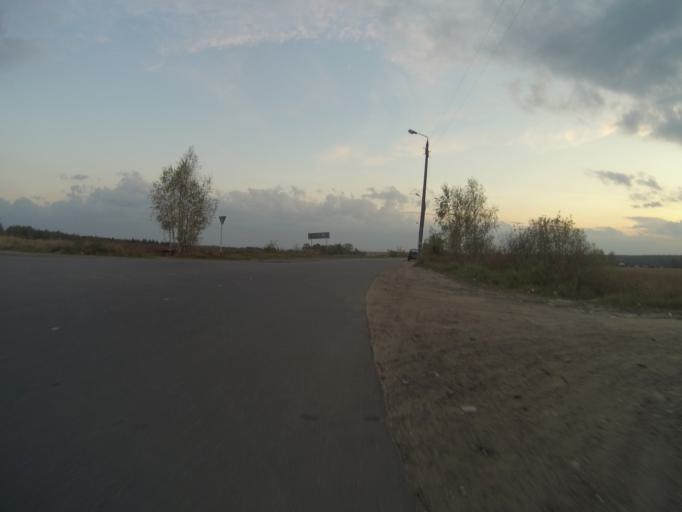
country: RU
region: Vladimir
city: Kommunar
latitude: 56.0721
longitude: 40.4904
